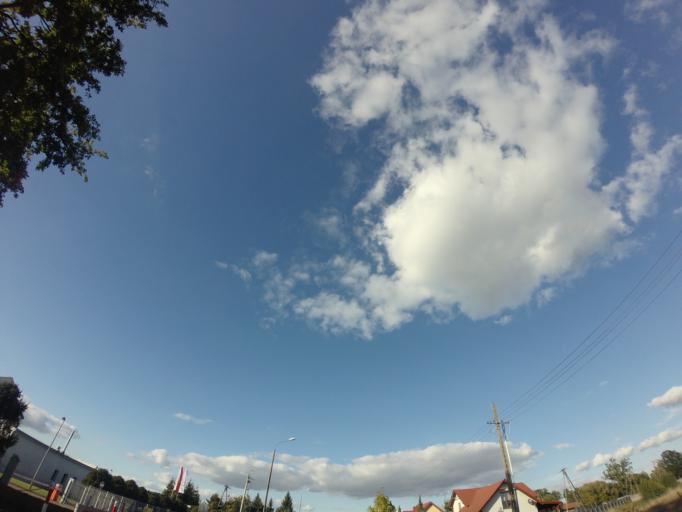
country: PL
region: Greater Poland Voivodeship
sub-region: Powiat nowotomyski
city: Nowy Tomysl
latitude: 52.2972
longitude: 16.1271
